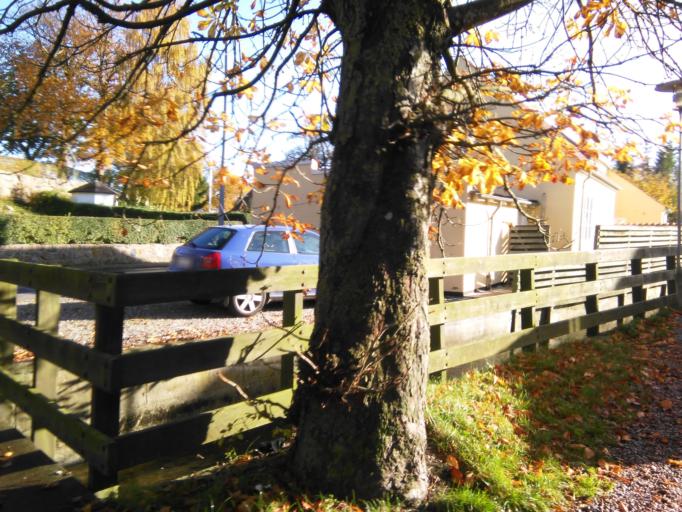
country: DK
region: Central Jutland
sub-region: Arhus Kommune
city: Marslet
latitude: 56.0673
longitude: 10.1602
